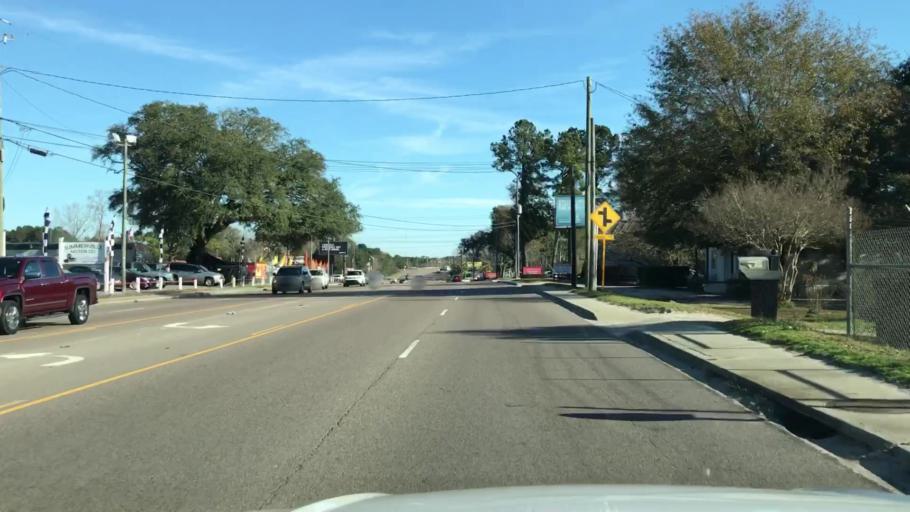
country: US
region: South Carolina
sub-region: Berkeley County
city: Ladson
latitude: 32.9933
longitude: -80.0987
